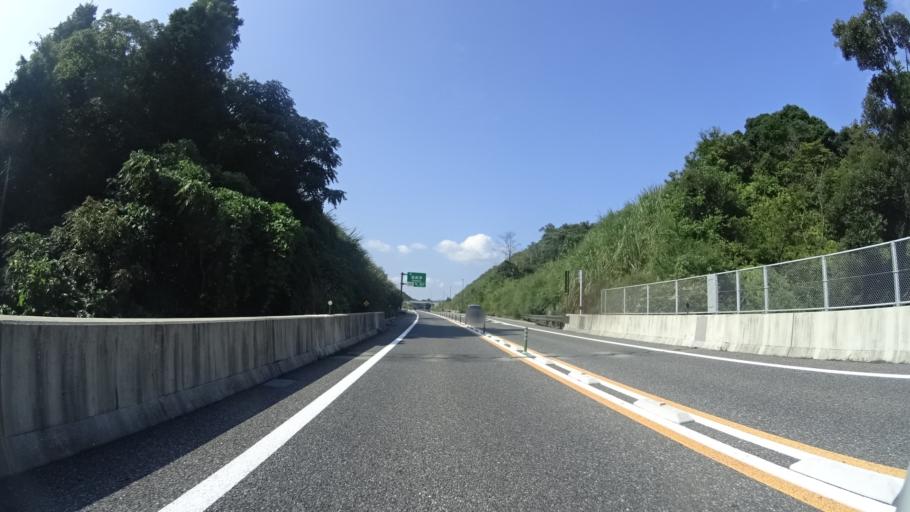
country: JP
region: Shimane
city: Gotsucho
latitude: 35.0851
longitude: 132.3477
